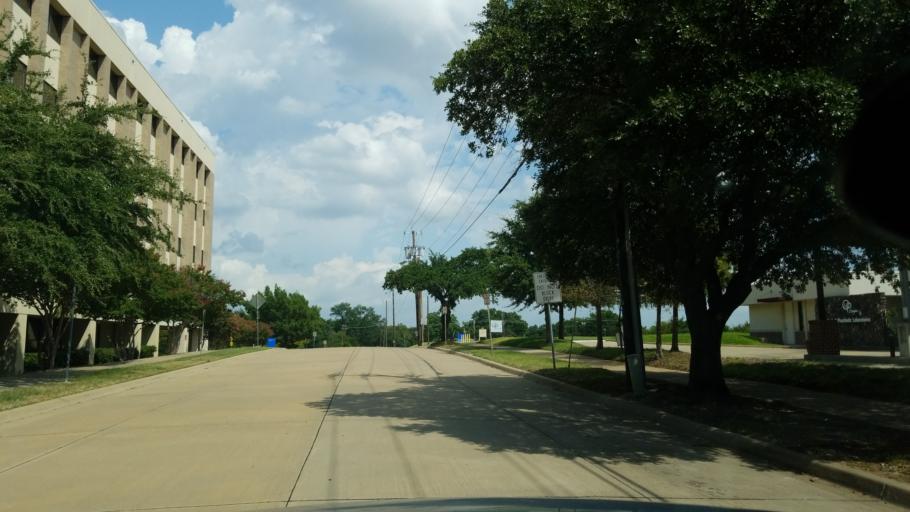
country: US
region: Texas
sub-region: Dallas County
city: Garland
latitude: 32.9186
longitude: -96.6616
